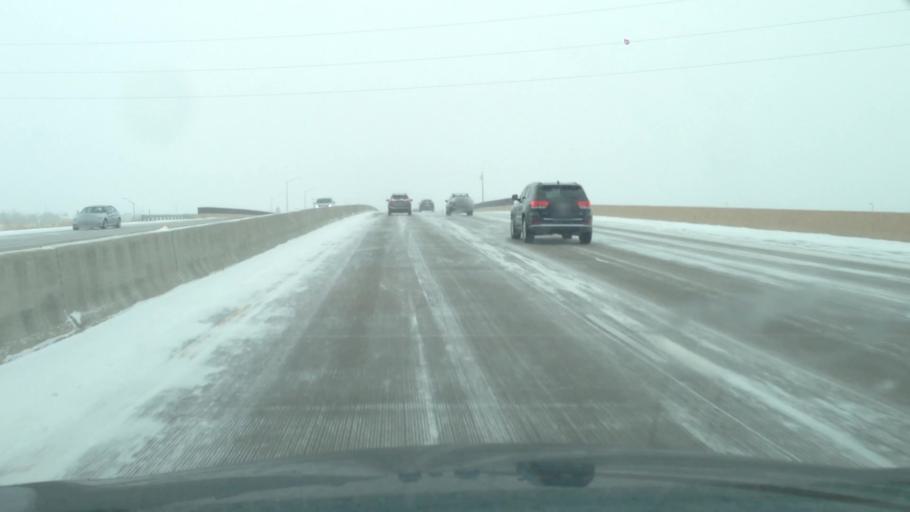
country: US
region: Colorado
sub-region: Arapahoe County
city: Dove Valley
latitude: 39.5963
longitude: -104.8030
